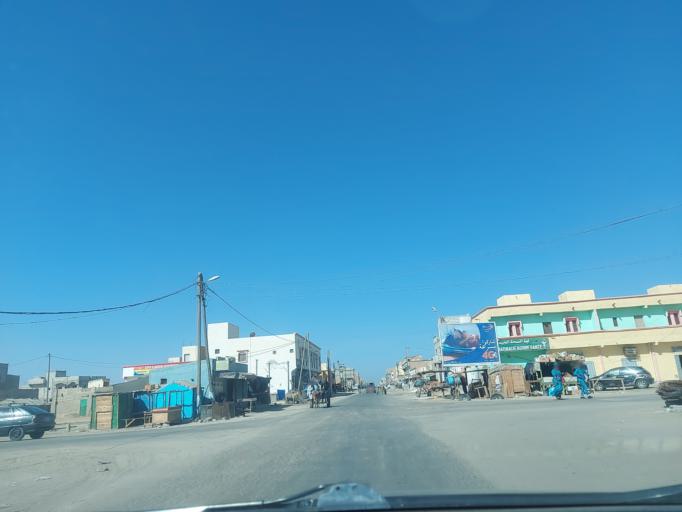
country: MR
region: Nouakchott
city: Nouakchott
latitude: 18.0665
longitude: -15.9972
